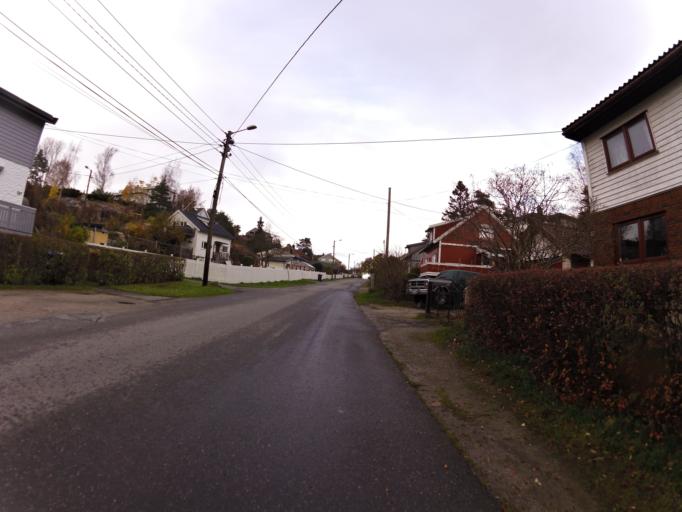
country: NO
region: Ostfold
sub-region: Fredrikstad
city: Fredrikstad
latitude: 59.2292
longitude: 10.9214
